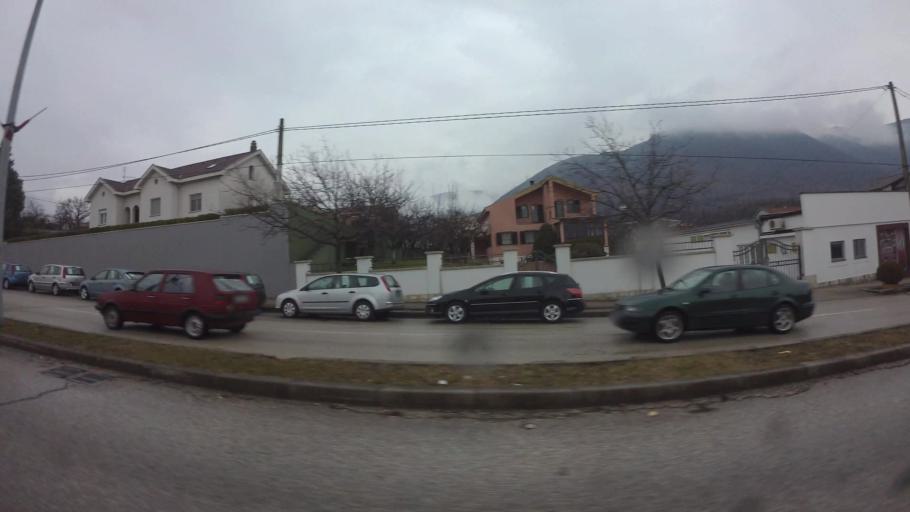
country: BA
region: Federation of Bosnia and Herzegovina
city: Cim
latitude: 43.3511
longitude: 17.7912
